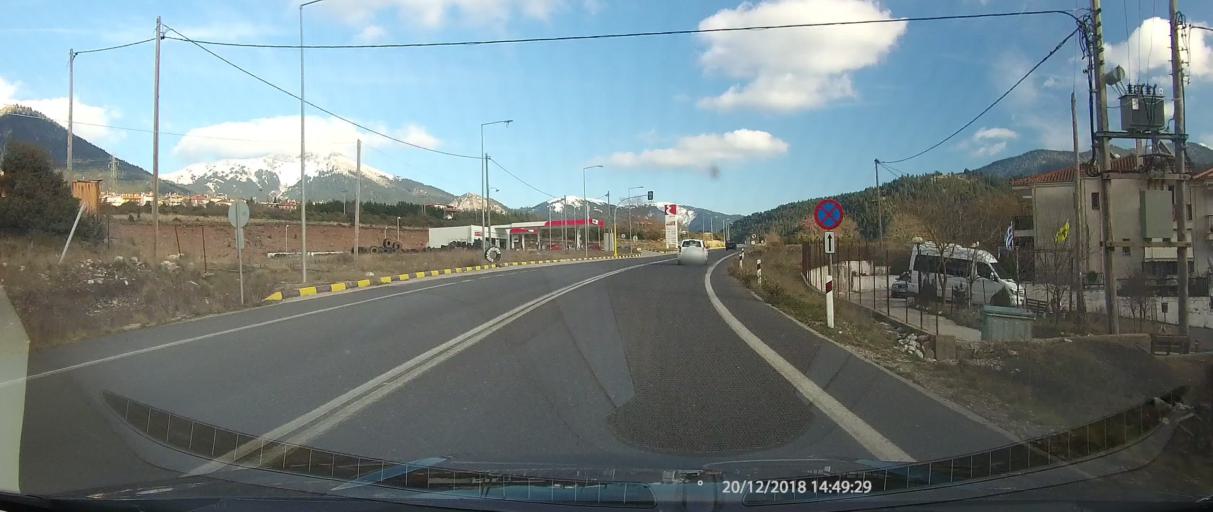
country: GR
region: Central Greece
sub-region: Nomos Evrytanias
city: Karpenisi
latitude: 38.9045
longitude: 21.8056
